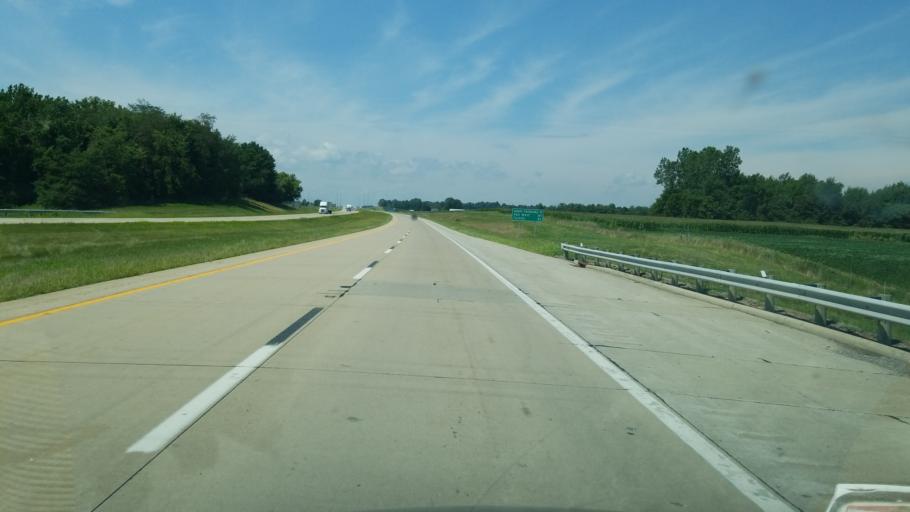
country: US
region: Ohio
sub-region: Wyandot County
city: Upper Sandusky
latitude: 40.8079
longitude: -83.1469
